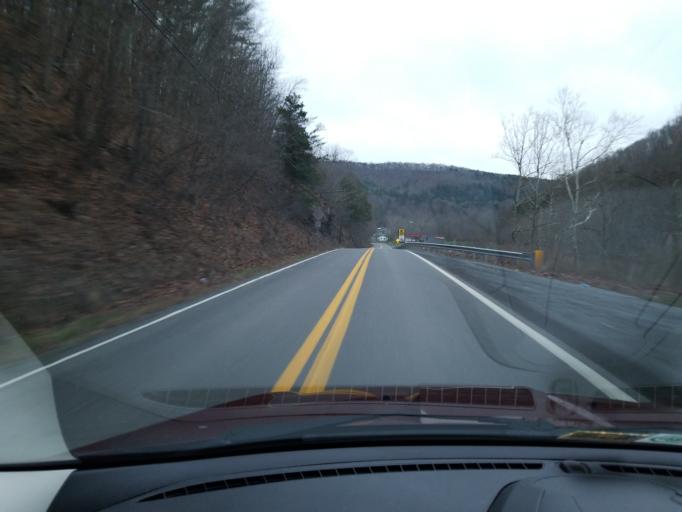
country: US
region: West Virginia
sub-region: Monroe County
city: Union
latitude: 37.5131
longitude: -80.6137
